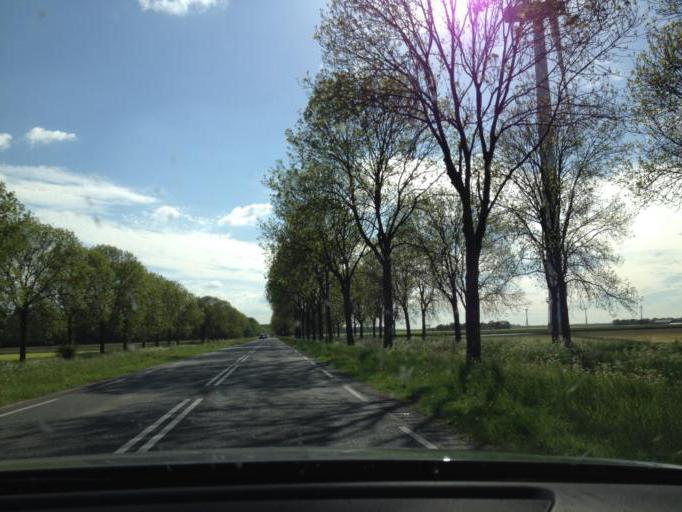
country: NL
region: Utrecht
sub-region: Gemeente Bunschoten
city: Bunschoten
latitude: 52.2742
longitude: 5.4108
